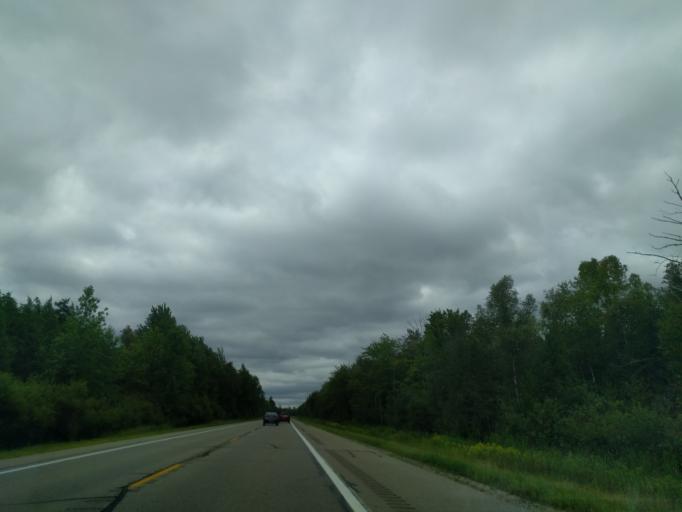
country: US
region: Michigan
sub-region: Delta County
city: Escanaba
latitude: 45.6073
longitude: -87.2207
